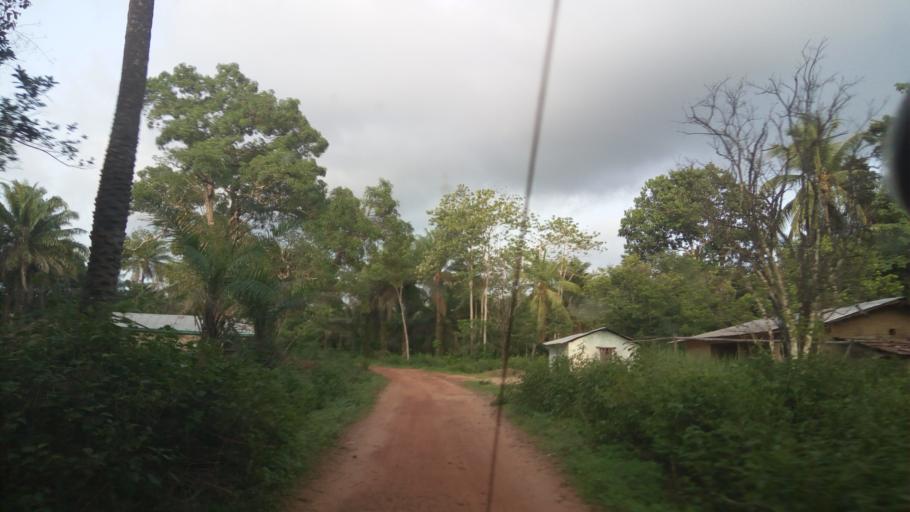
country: SL
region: Northern Province
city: Mambolo
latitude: 9.0241
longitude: -13.0316
